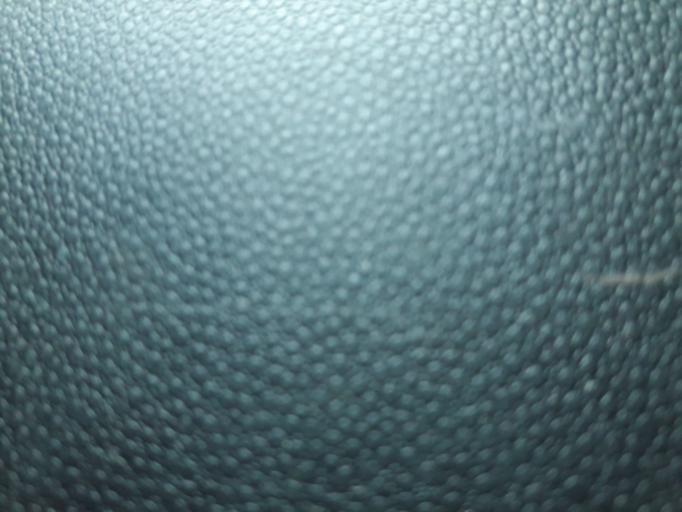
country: CA
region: Newfoundland and Labrador
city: St. John's
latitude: 47.5703
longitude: -52.7008
